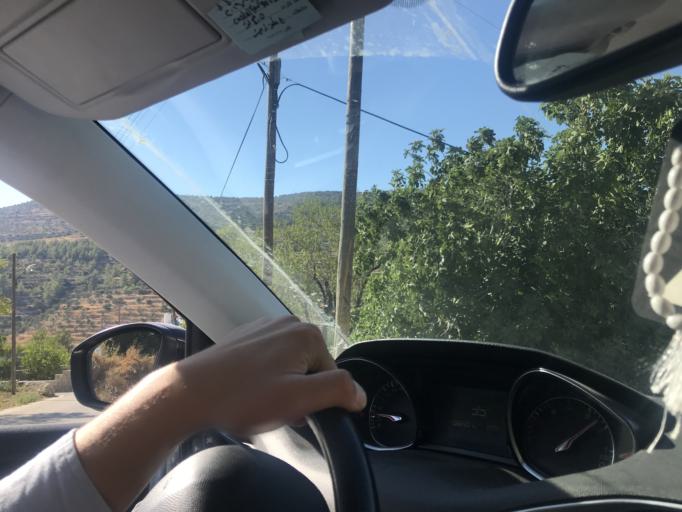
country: PS
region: West Bank
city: Bani Zayd ash Sharqiyah
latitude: 32.0628
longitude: 35.1768
